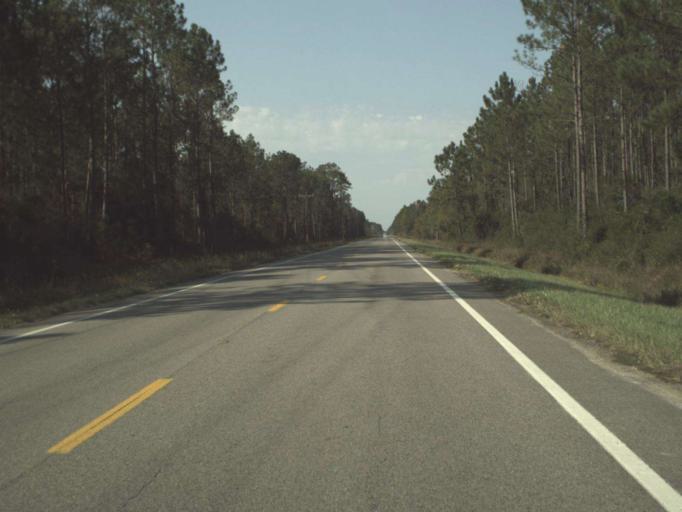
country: US
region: Florida
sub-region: Gulf County
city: Wewahitchka
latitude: 29.9899
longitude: -85.1693
